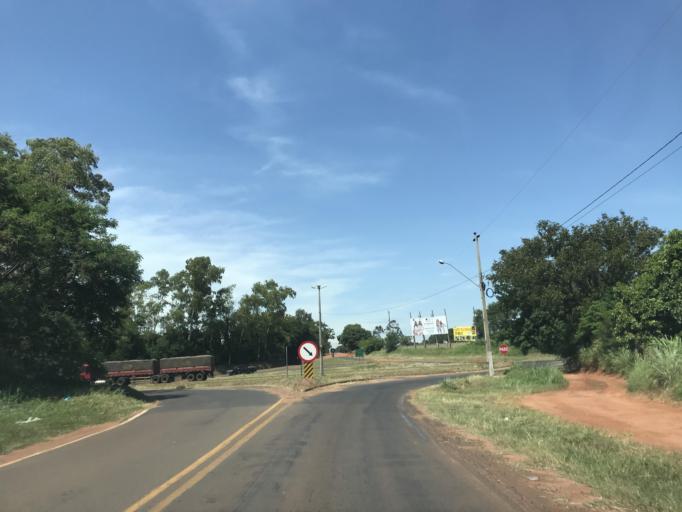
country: BR
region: Parana
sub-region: Paranavai
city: Nova Aurora
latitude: -22.9535
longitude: -52.7009
